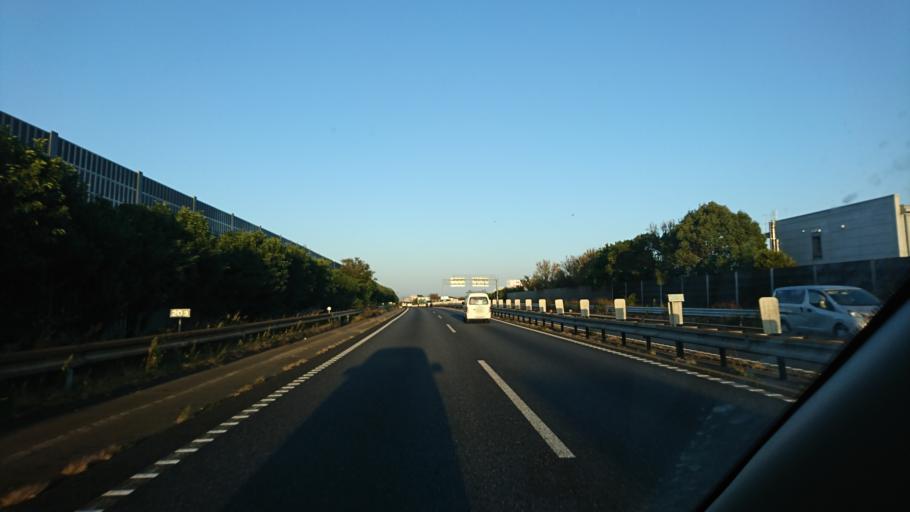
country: JP
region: Hyogo
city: Akashi
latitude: 34.7131
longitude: 134.9378
